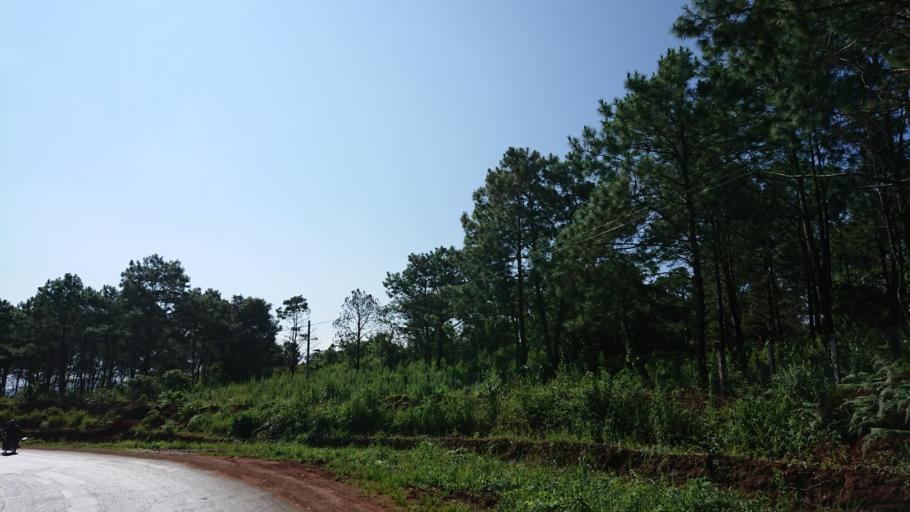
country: MM
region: Shan
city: Taunggyi
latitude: 20.7468
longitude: 97.0895
